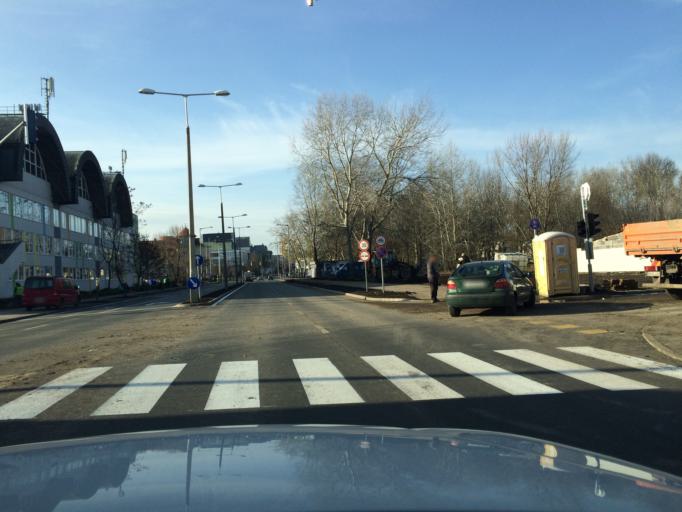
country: HU
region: Szabolcs-Szatmar-Bereg
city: Nyiregyhaza
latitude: 47.9572
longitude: 21.7241
